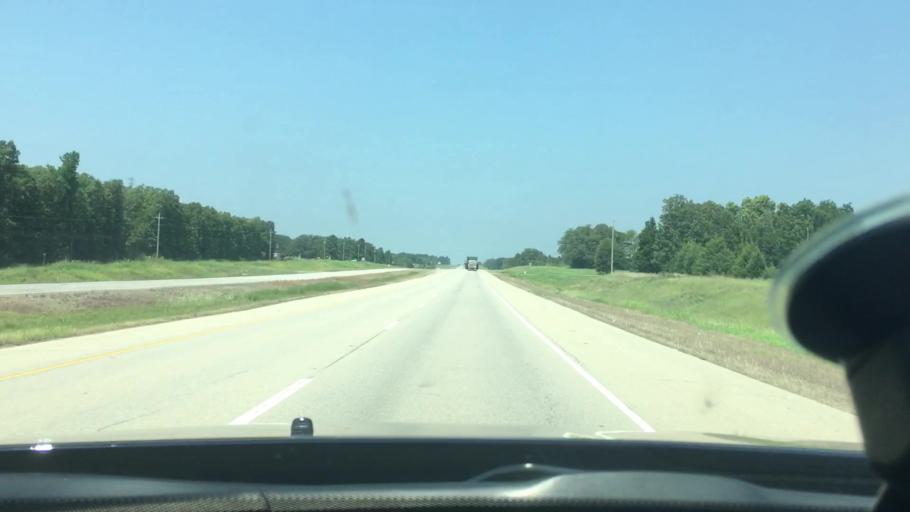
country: US
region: Oklahoma
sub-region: Atoka County
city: Atoka
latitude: 34.3179
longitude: -96.0332
